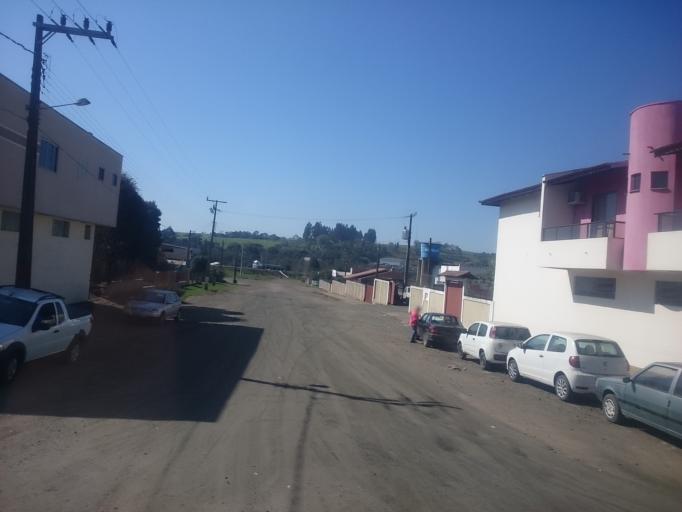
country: BR
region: Santa Catarina
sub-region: Canoinhas
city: Canoinhas
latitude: -26.3967
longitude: -50.1614
